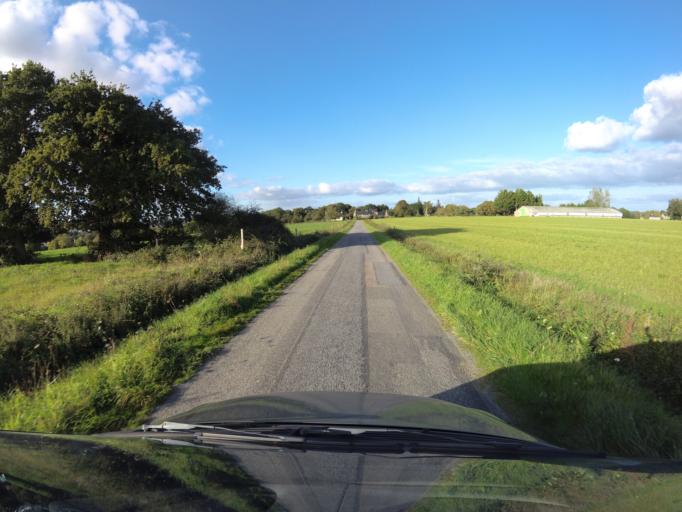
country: FR
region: Brittany
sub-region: Departement du Morbihan
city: Peillac
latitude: 47.7187
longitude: -2.1932
